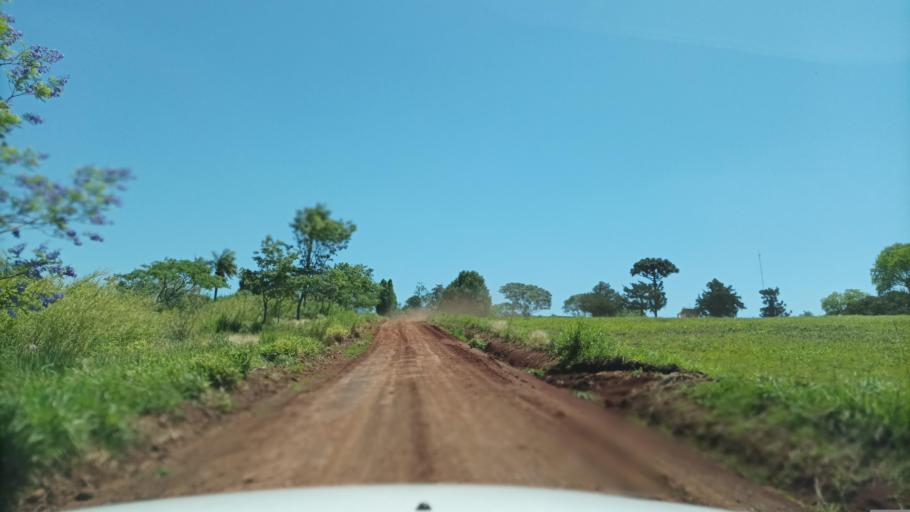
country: AR
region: Misiones
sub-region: Departamento de Apostoles
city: San Jose
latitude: -27.7911
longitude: -55.7131
